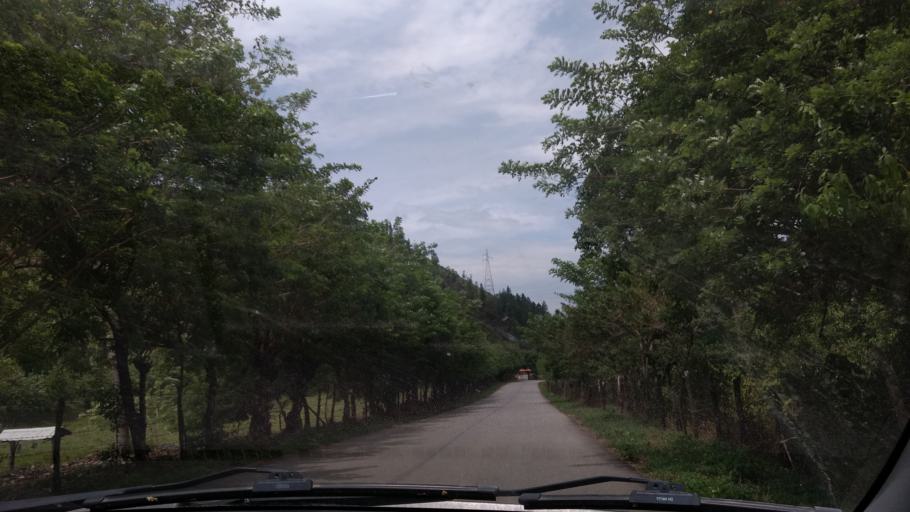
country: CO
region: Cauca
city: Buenos Aires
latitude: 3.0761
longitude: -76.6517
